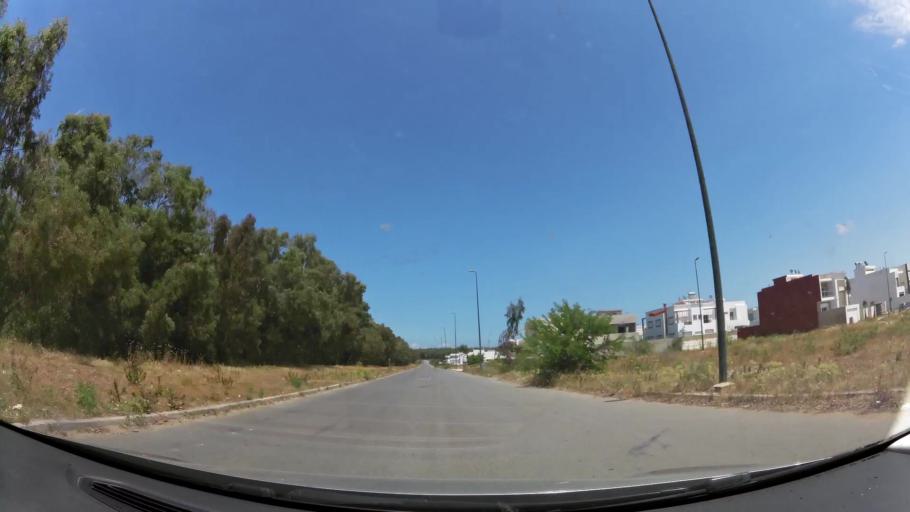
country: MA
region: Gharb-Chrarda-Beni Hssen
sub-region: Kenitra Province
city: Kenitra
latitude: 34.2653
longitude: -6.6312
